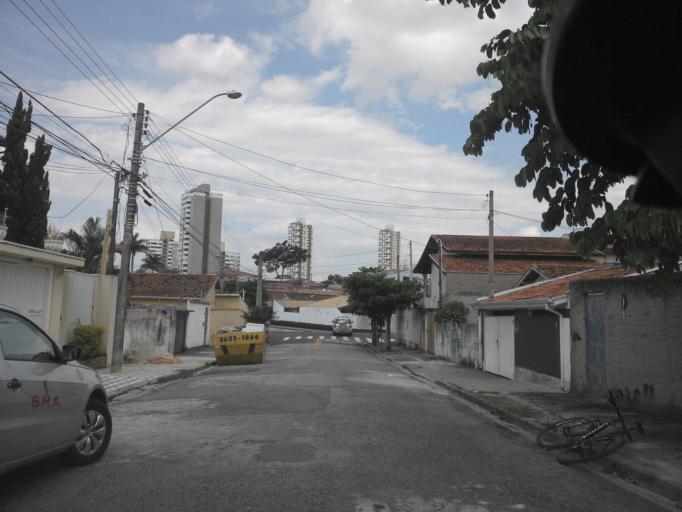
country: BR
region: Sao Paulo
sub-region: Taubate
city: Taubate
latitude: -23.0379
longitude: -45.5717
